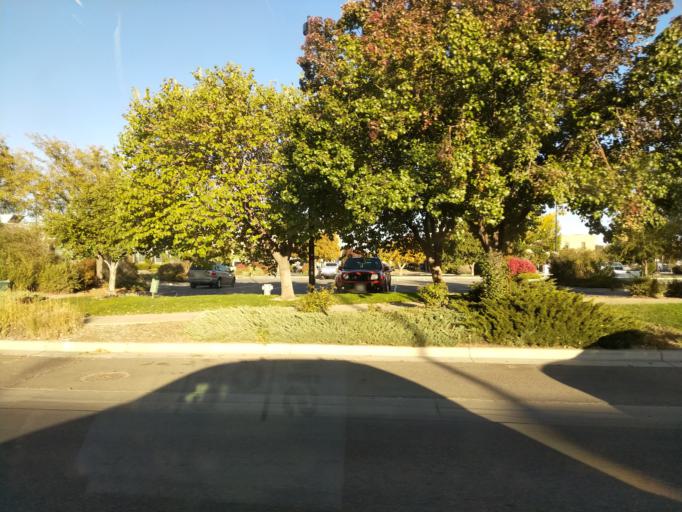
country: US
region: Colorado
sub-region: Mesa County
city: Grand Junction
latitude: 39.0662
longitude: -108.5709
